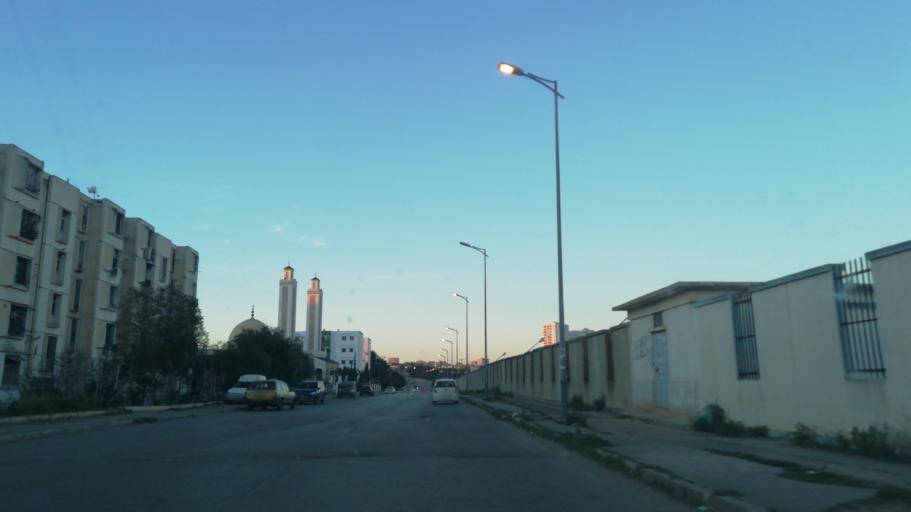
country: DZ
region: Oran
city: Bir el Djir
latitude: 35.7035
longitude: -0.5853
